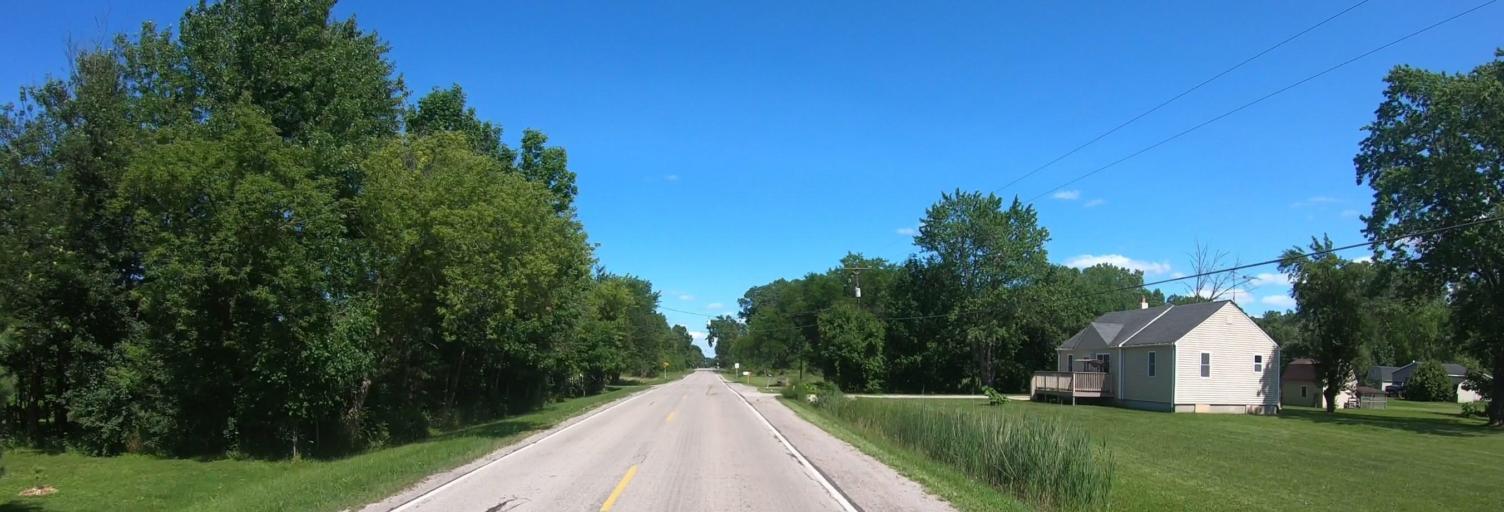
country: US
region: Michigan
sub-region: Genesee County
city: Flushing
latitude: 43.0785
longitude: -83.7914
